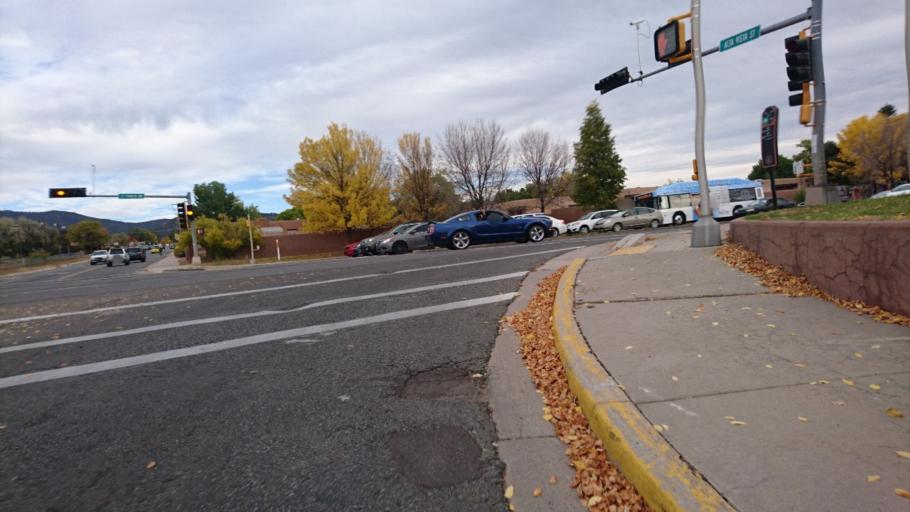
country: US
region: New Mexico
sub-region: Santa Fe County
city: Santa Fe
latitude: 35.6710
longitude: -105.9556
